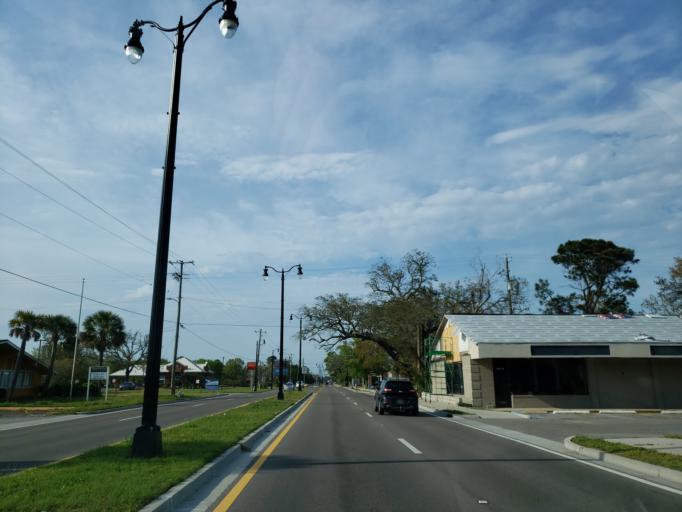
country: US
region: Mississippi
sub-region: Harrison County
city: Gulfport
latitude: 30.3838
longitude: -89.0440
